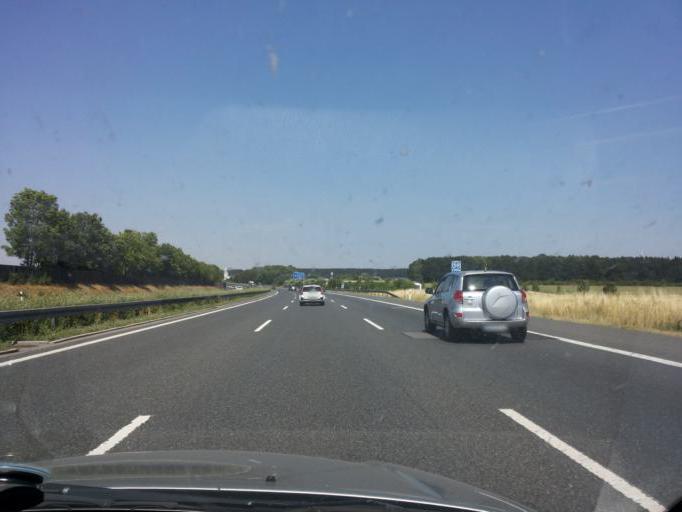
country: DE
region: Bavaria
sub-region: Upper Bavaria
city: Denkendorf
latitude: 48.9247
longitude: 11.4670
